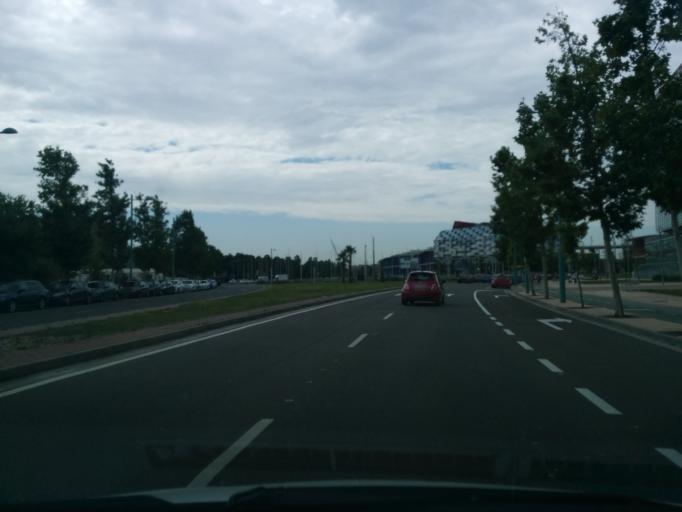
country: ES
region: Aragon
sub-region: Provincia de Zaragoza
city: Almozara
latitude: 41.6736
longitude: -0.8980
